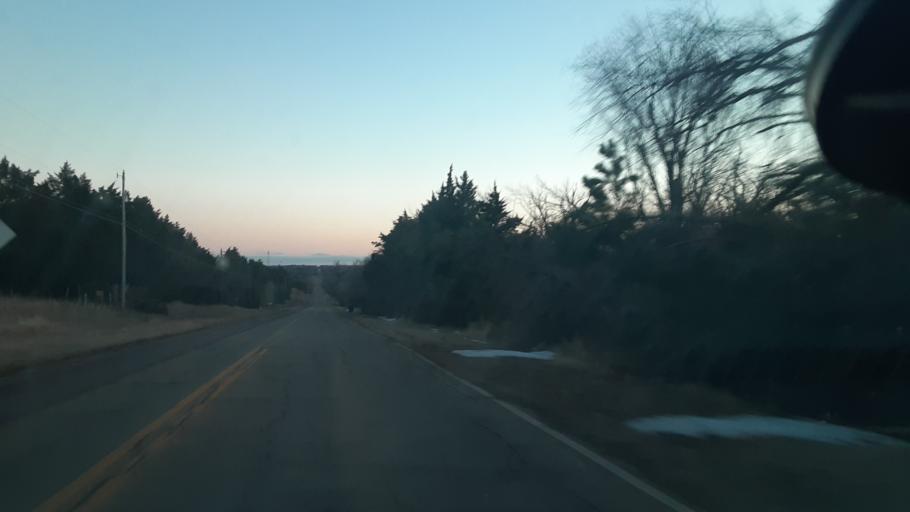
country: US
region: Oklahoma
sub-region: Oklahoma County
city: Edmond
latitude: 35.7235
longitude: -97.4252
